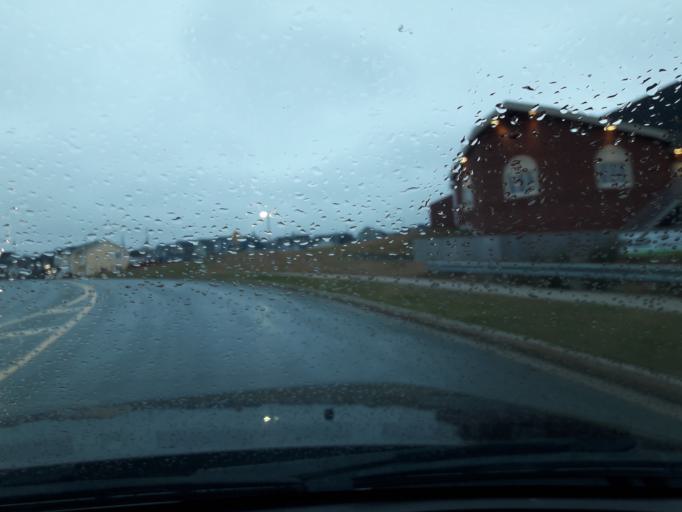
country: CA
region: Newfoundland and Labrador
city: Mount Pearl
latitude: 47.5482
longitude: -52.7851
